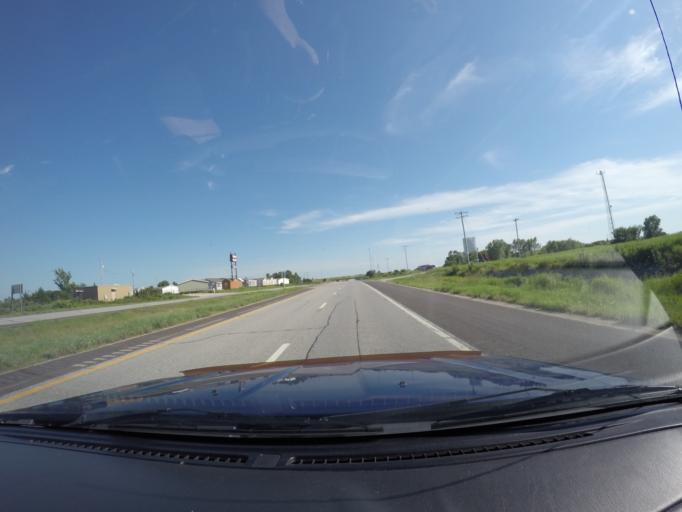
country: US
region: Kansas
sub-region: Riley County
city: Manhattan
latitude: 39.0662
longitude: -96.5385
